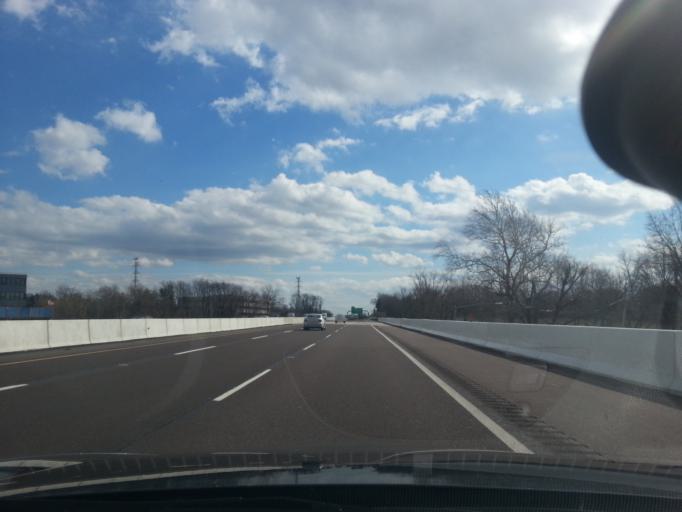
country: US
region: Pennsylvania
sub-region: Montgomery County
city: Blue Bell
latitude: 40.1504
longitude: -75.2921
